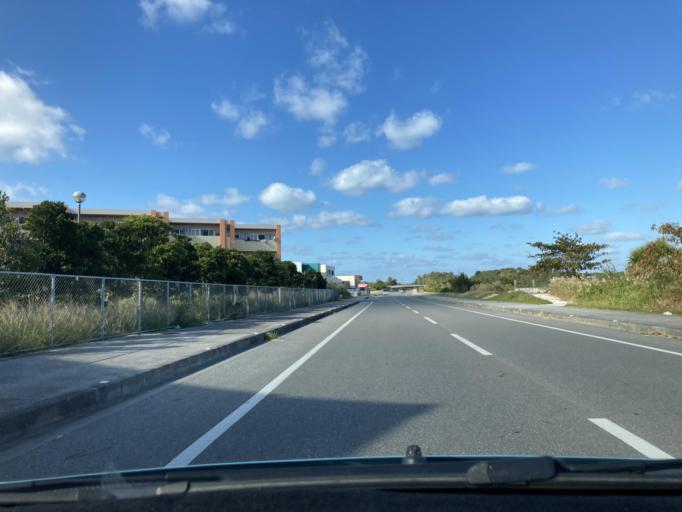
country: JP
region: Okinawa
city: Katsuren-haebaru
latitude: 26.3115
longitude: 127.9196
